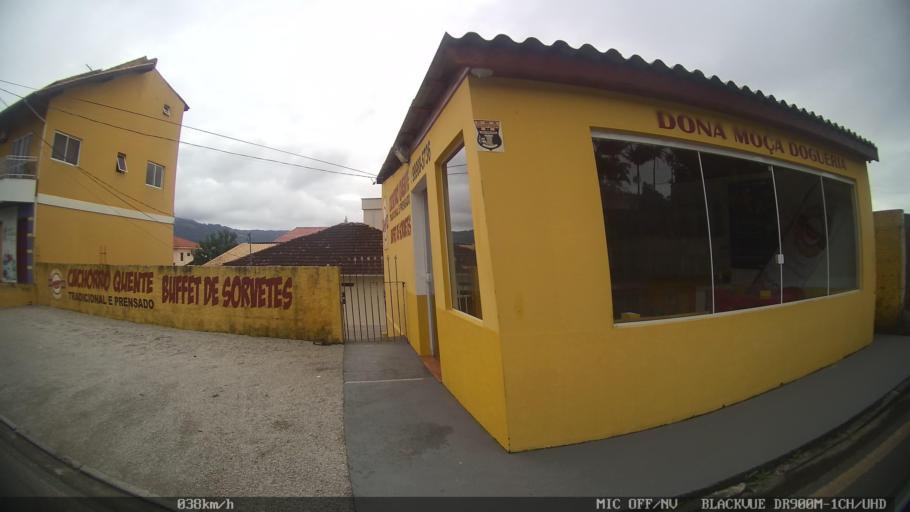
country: BR
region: Santa Catarina
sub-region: Biguacu
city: Biguacu
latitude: -27.5349
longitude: -48.6322
